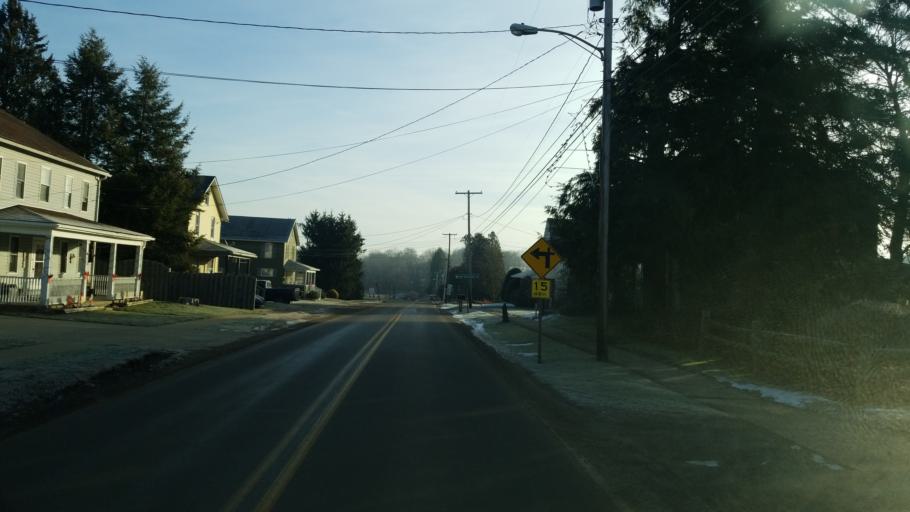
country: US
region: Pennsylvania
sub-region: Indiana County
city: Chevy Chase Heights
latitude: 40.8805
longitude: -79.2362
